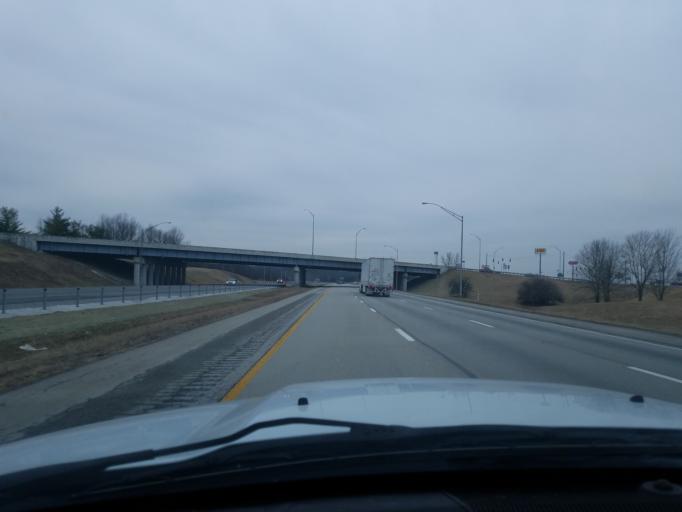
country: US
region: Kentucky
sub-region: Hardin County
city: Elizabethtown
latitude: 37.7151
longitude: -85.8294
